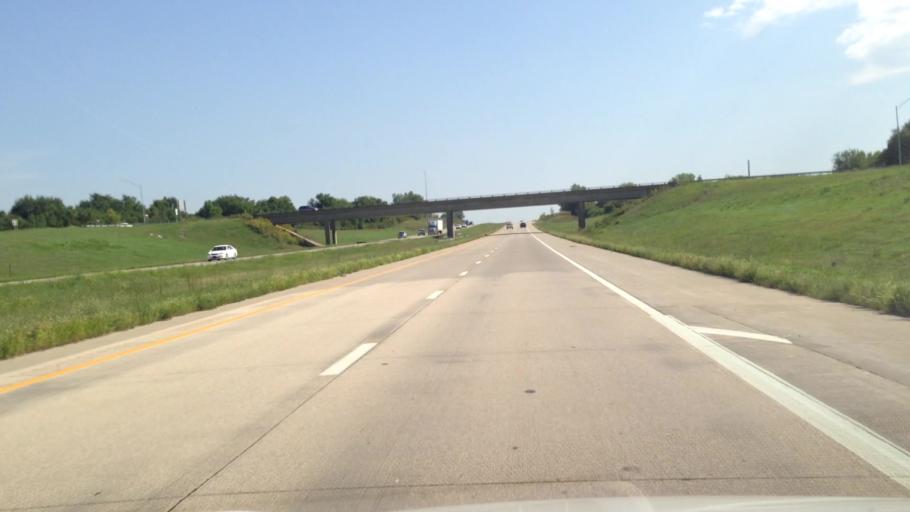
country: US
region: Kansas
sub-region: Miami County
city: Louisburg
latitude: 38.5650
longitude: -94.6945
